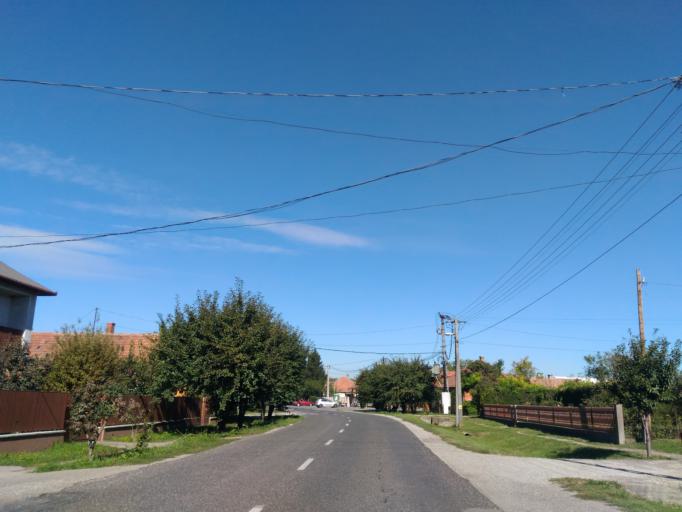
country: HU
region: Fejer
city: Ivancsa
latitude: 47.1609
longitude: 18.8269
